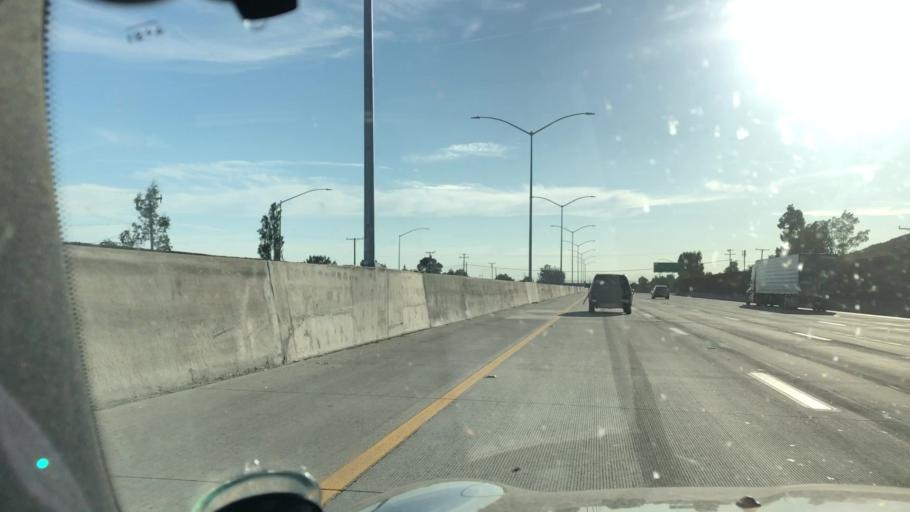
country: US
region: California
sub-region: Riverside County
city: Glen Avon
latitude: 34.0191
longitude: -117.4998
